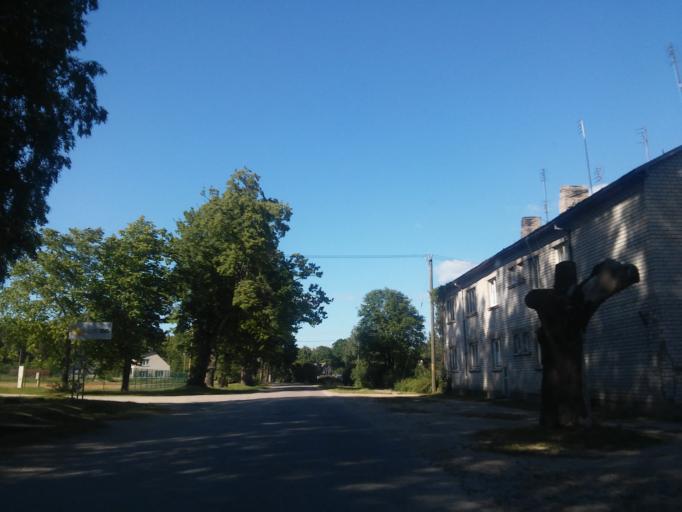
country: LV
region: Vainode
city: Vainode
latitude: 56.4318
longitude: 21.8714
